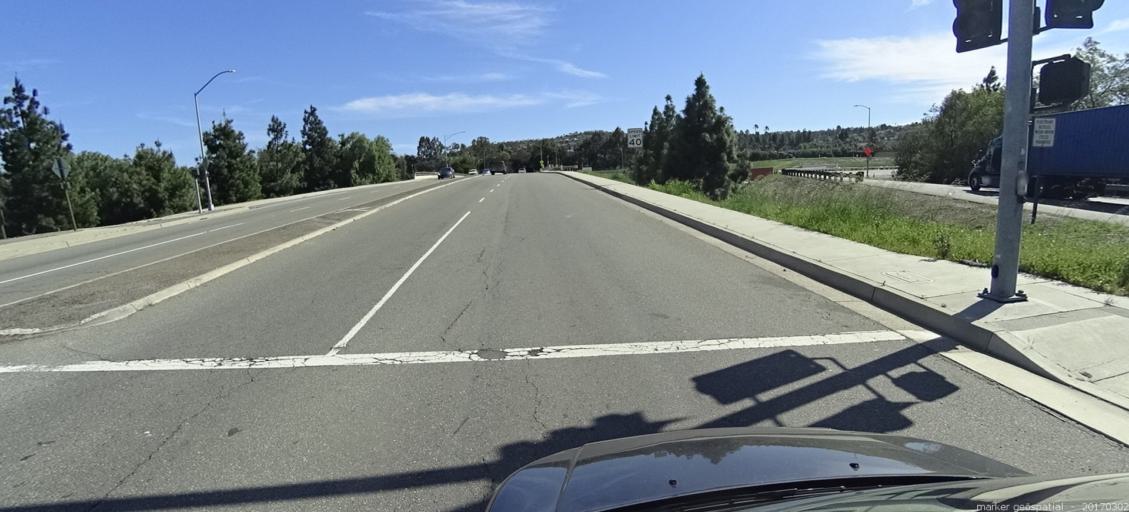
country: US
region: California
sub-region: Orange County
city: Yorba Linda
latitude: 33.8520
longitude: -117.8154
